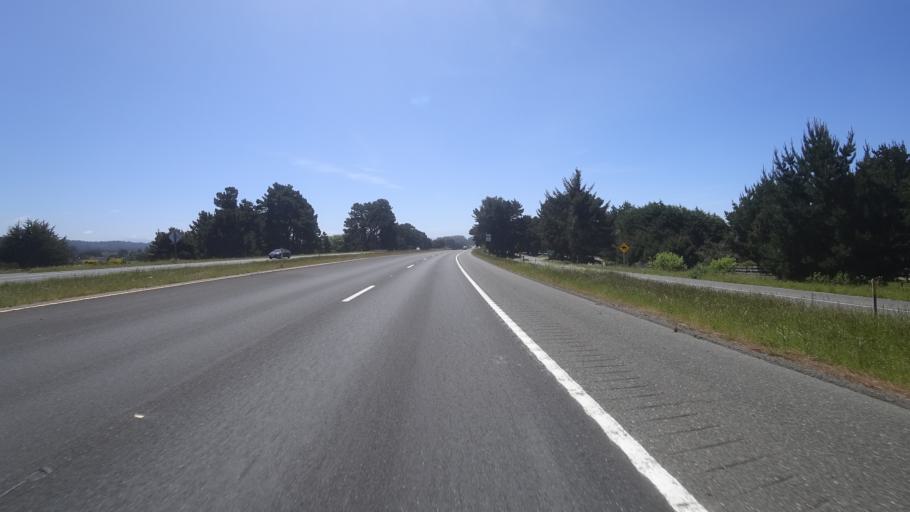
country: US
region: California
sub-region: Humboldt County
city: McKinleyville
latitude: 40.9707
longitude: -124.1163
